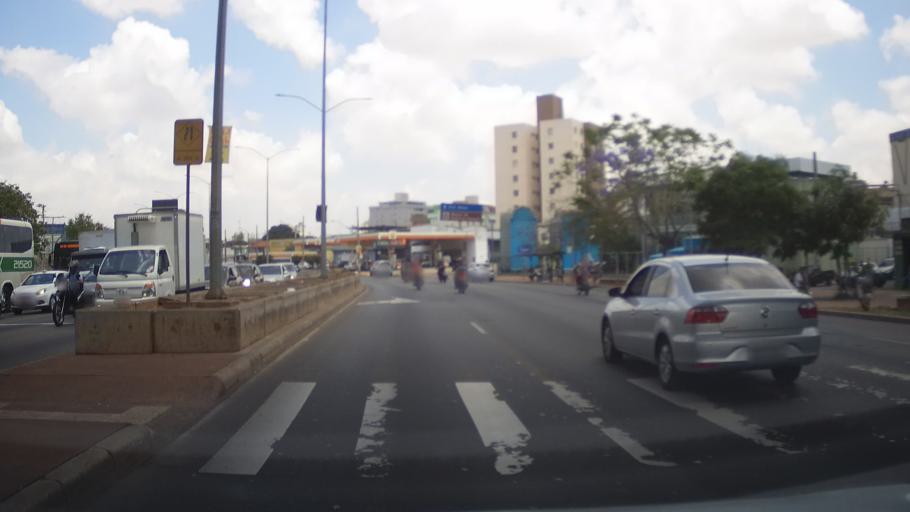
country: BR
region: Minas Gerais
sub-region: Belo Horizonte
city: Belo Horizonte
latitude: -19.9189
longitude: -43.9683
